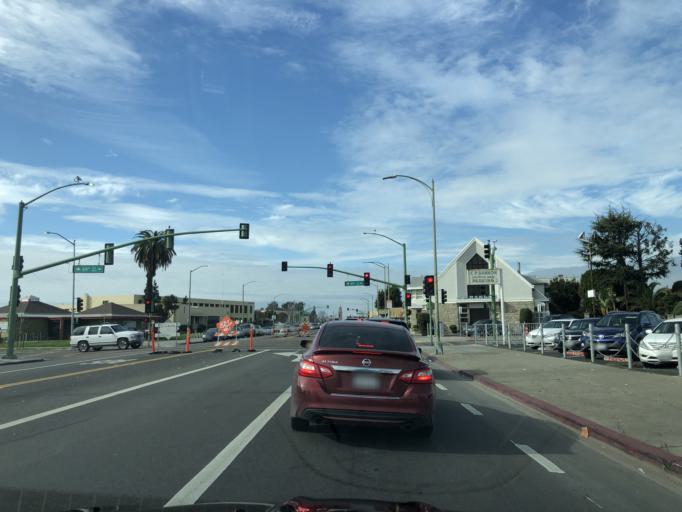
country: US
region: California
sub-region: Alameda County
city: San Leandro
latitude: 37.7606
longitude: -122.1896
